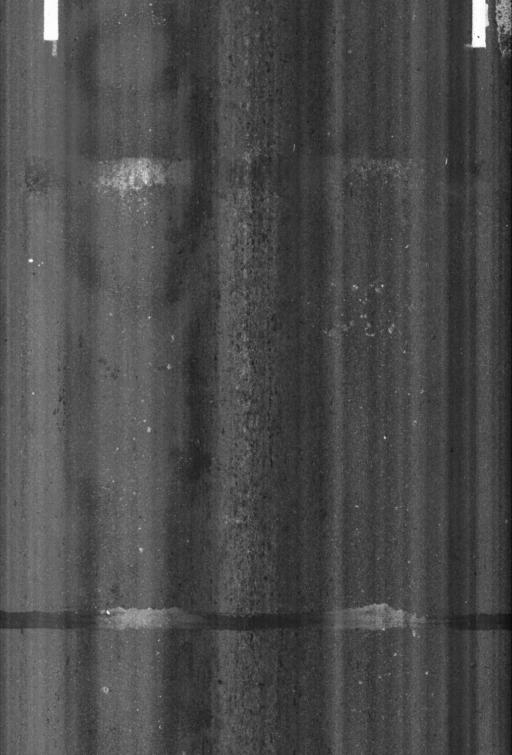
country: US
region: Maryland
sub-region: Prince George's County
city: Capitol Heights
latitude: 38.8899
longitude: -76.9363
